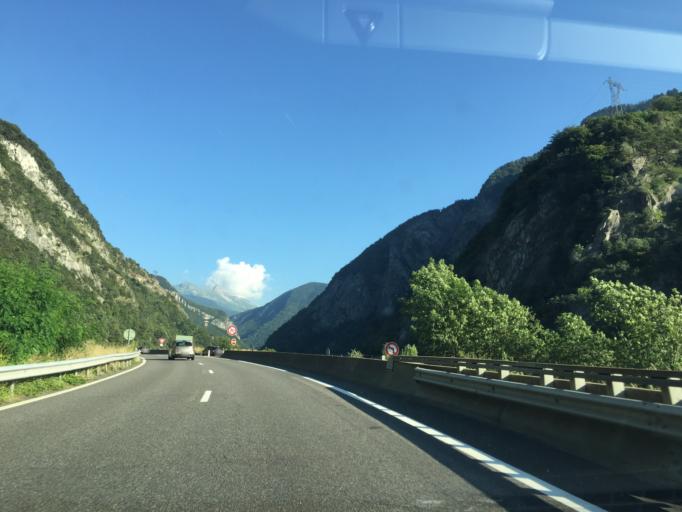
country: FR
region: Rhone-Alpes
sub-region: Departement de la Savoie
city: Aigueblanche
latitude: 45.4978
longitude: 6.5130
